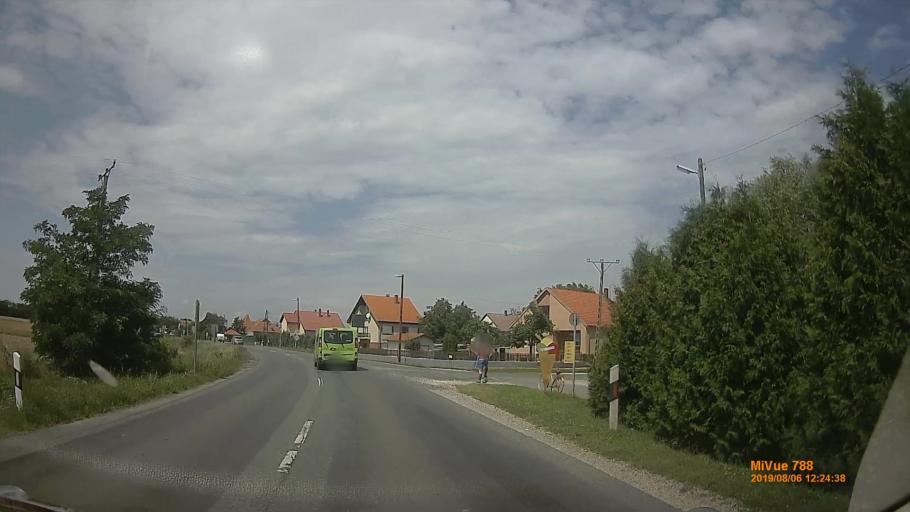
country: HU
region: Vas
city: Taplanszentkereszt
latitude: 47.1943
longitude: 16.6965
